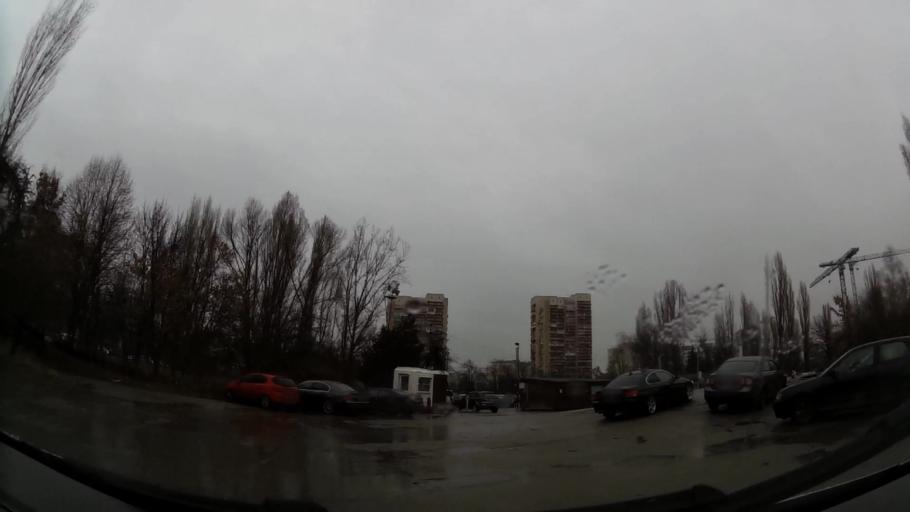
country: BG
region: Sofia-Capital
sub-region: Stolichna Obshtina
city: Sofia
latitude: 42.6600
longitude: 23.3517
